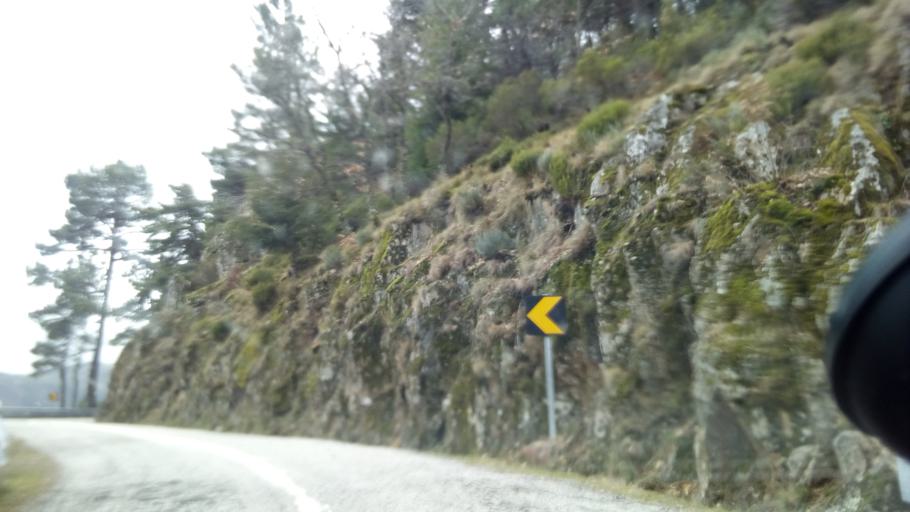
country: PT
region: Guarda
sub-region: Manteigas
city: Manteigas
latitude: 40.4161
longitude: -7.5388
